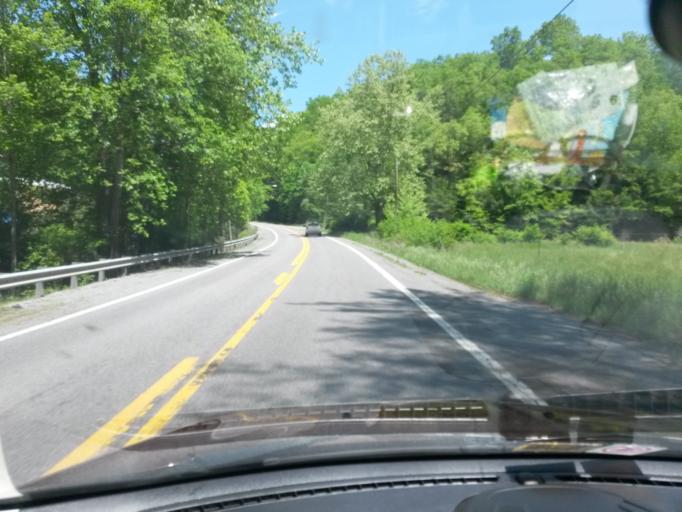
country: US
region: West Virginia
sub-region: McDowell County
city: Welch
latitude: 37.4724
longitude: -81.5419
